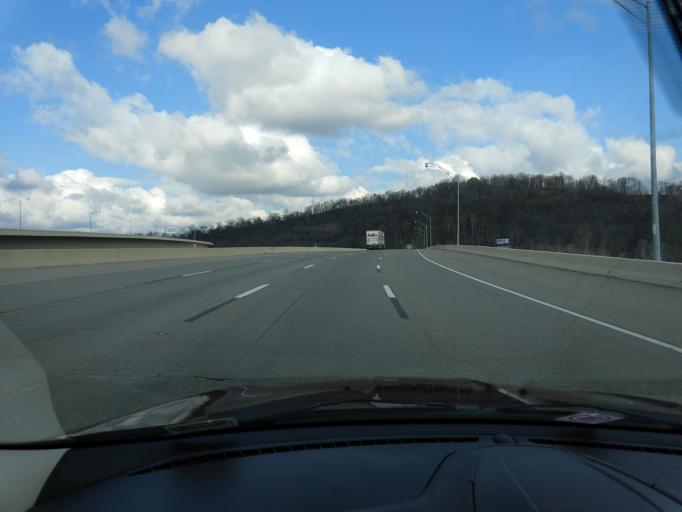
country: US
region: West Virginia
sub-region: Kanawha County
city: South Charleston
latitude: 38.3613
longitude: -81.7151
